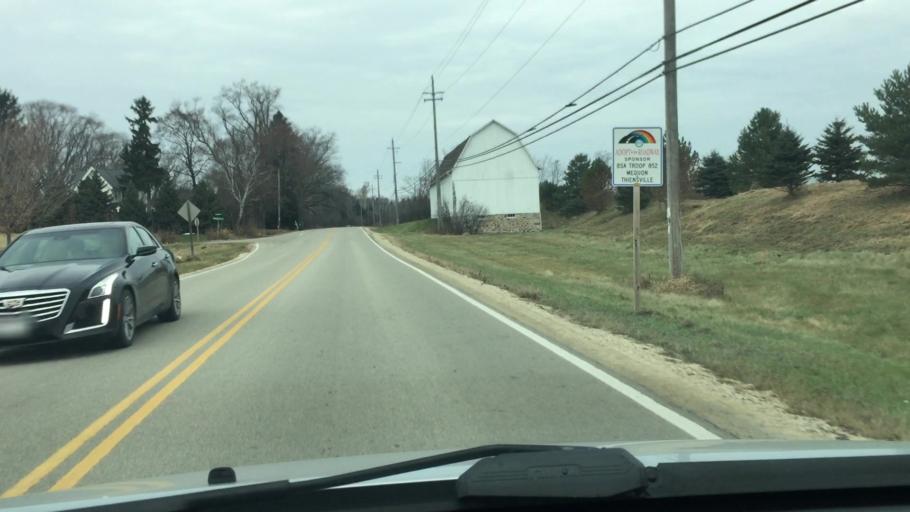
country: US
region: Wisconsin
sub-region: Ozaukee County
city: Thiensville
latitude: 43.2518
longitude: -87.9820
